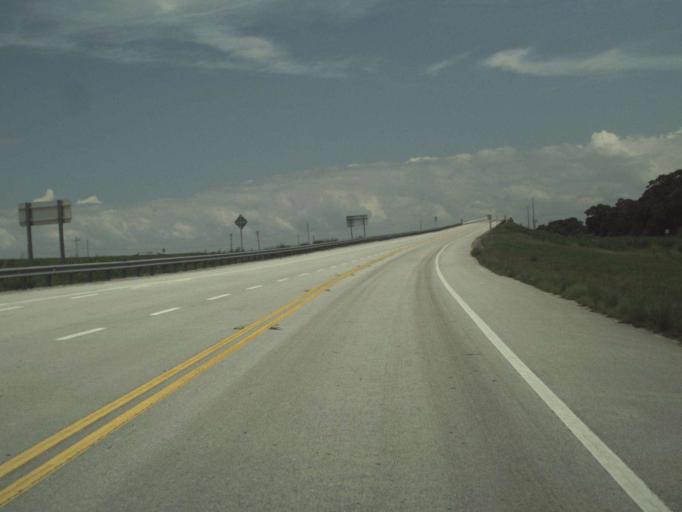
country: US
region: Florida
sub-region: Martin County
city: Indiantown
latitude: 26.9792
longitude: -80.6151
